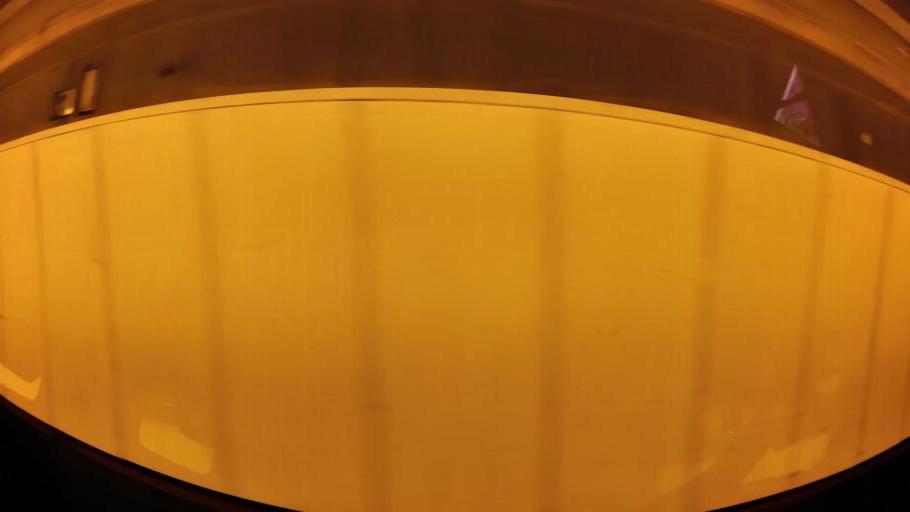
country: CL
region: Santiago Metropolitan
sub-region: Provincia de Santiago
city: Santiago
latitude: -33.4132
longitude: -70.6143
